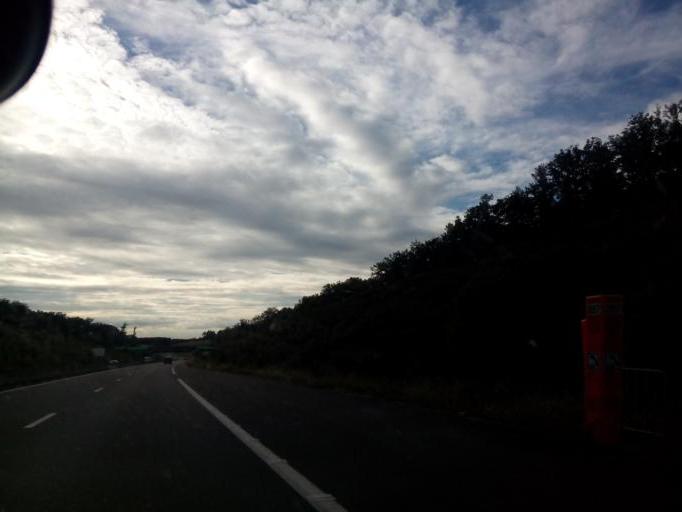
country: FR
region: Centre
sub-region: Departement d'Indre-et-Loire
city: Montbazon
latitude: 47.3031
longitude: 0.6808
